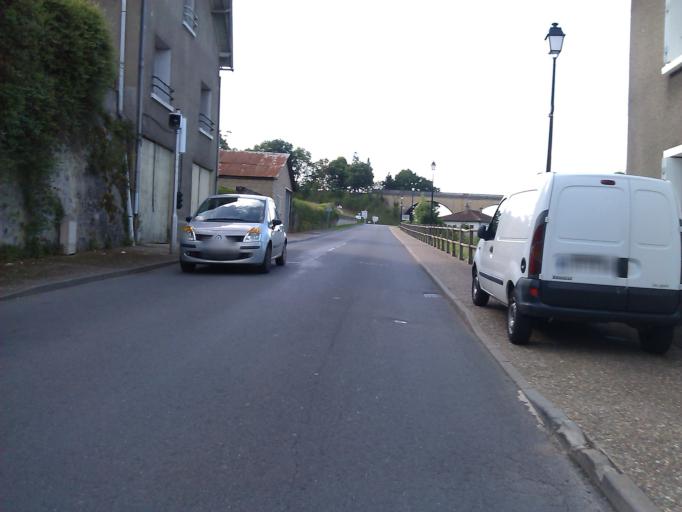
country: FR
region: Poitou-Charentes
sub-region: Departement de la Vienne
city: Availles-Limouzine
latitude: 46.2316
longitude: 0.6786
